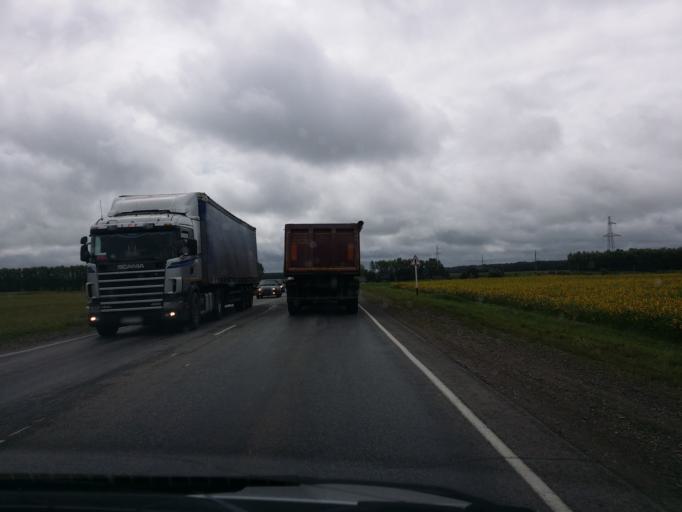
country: RU
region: Altai Krai
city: Zonal'noye
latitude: 52.8477
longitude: 84.8591
